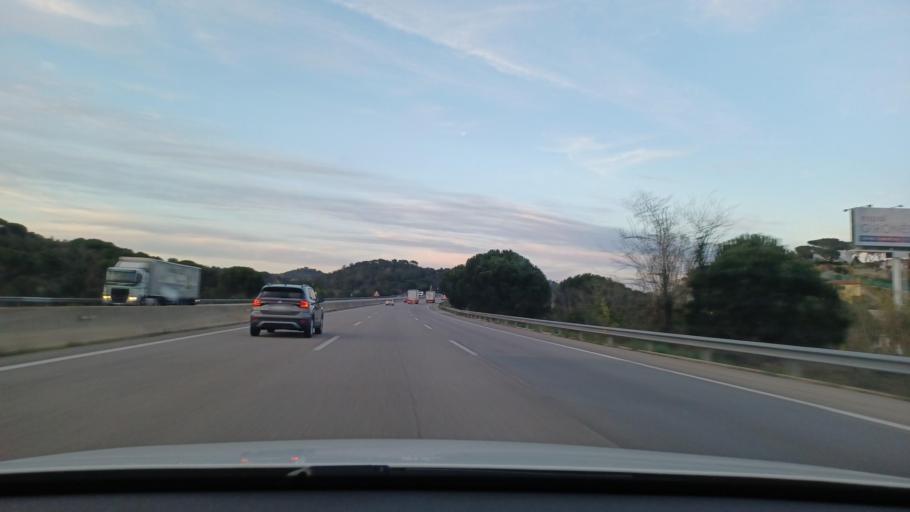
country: ES
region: Catalonia
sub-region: Provincia de Girona
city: Macanet de la Selva
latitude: 41.7547
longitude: 2.7113
